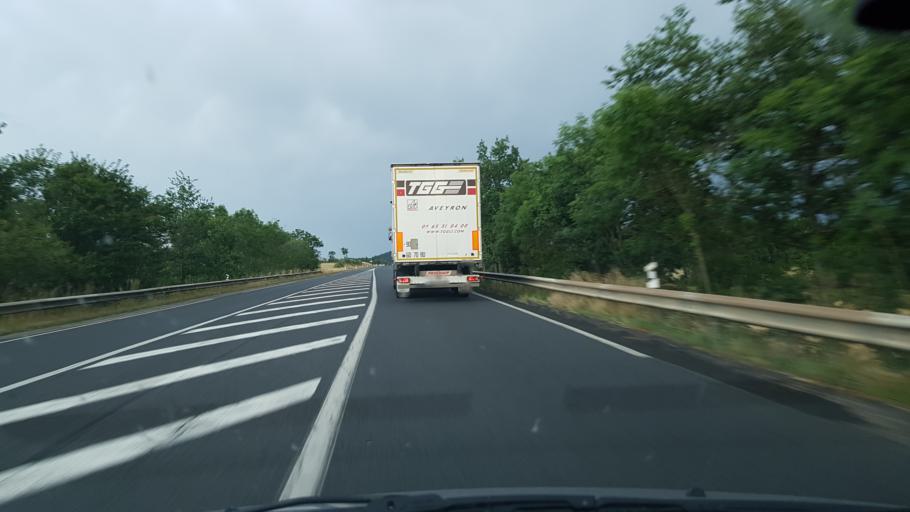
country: FR
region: Auvergne
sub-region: Departement de la Haute-Loire
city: Paulhaguet
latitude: 45.1400
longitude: 3.5828
